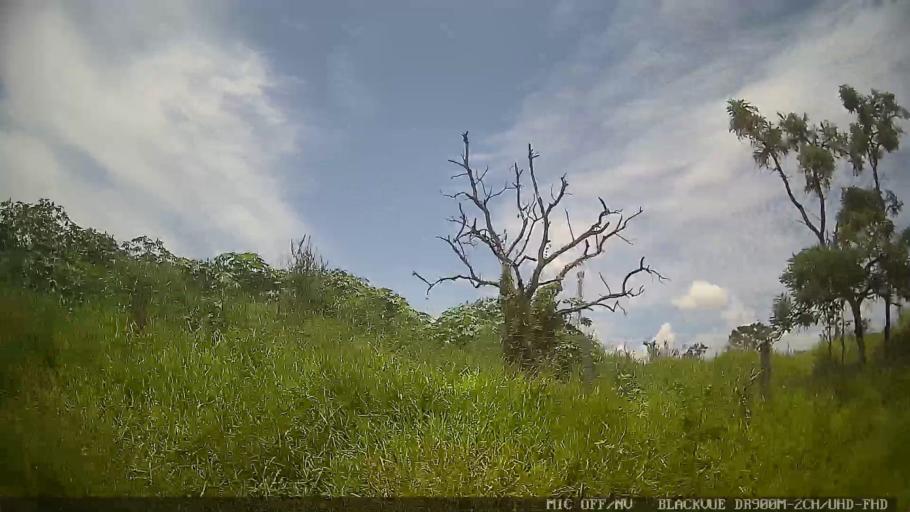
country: BR
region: Sao Paulo
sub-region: Jarinu
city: Jarinu
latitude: -23.0645
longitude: -46.6395
